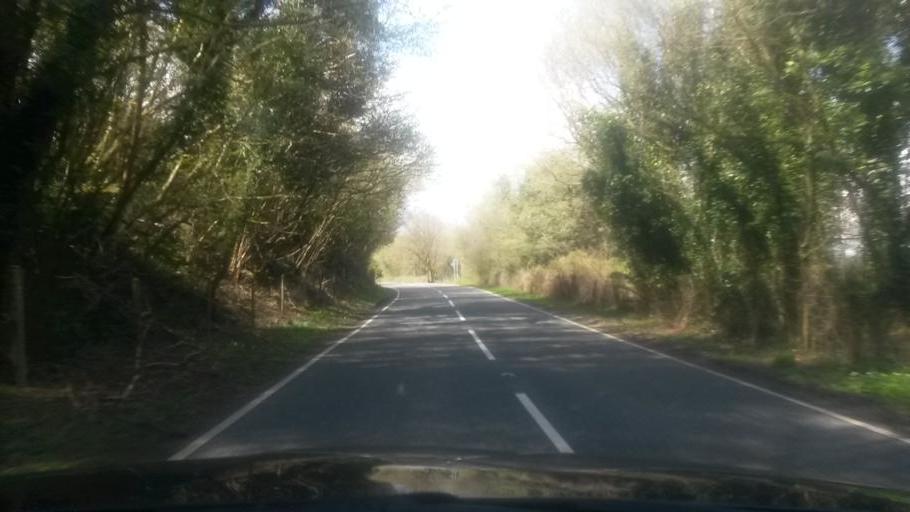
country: GB
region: Northern Ireland
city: Irvinestown
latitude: 54.4166
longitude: -7.7304
